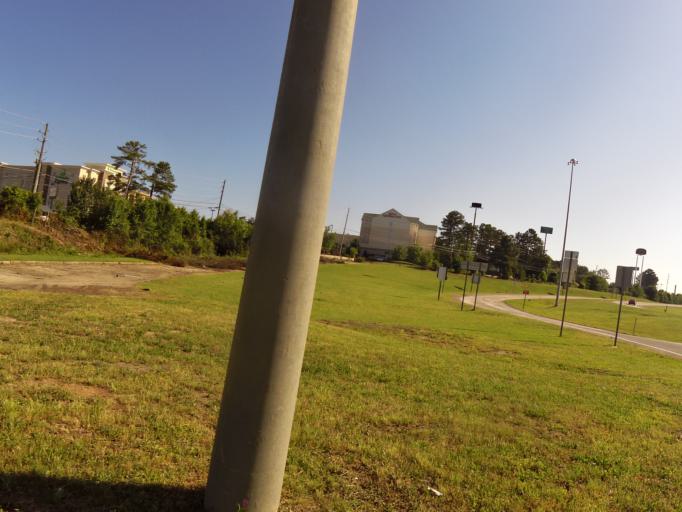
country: US
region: Georgia
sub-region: Columbia County
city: Martinez
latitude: 33.5125
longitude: -82.0449
